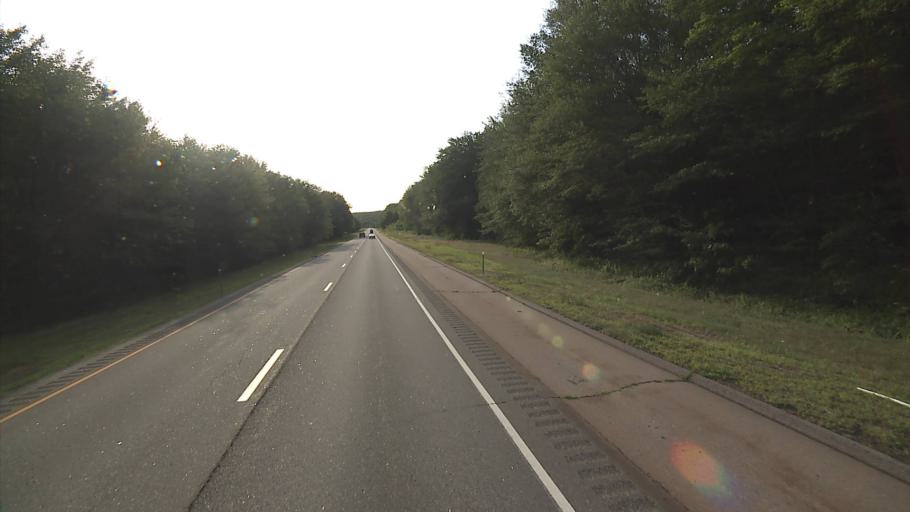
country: US
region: Connecticut
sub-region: New London County
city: Colchester
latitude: 41.5664
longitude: -72.2559
